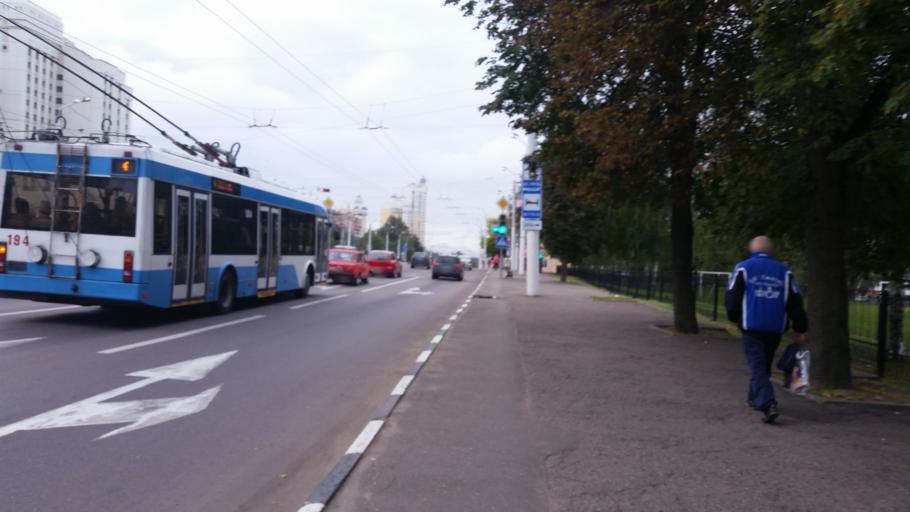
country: BY
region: Vitebsk
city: Vitebsk
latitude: 55.1744
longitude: 30.1996
